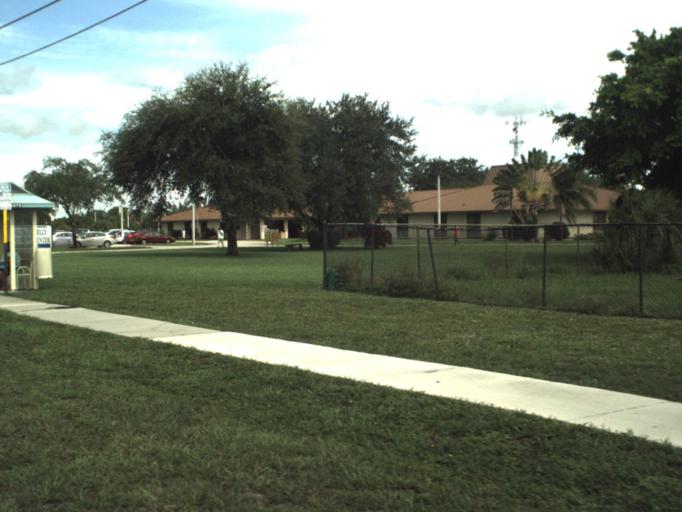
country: US
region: Florida
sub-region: Palm Beach County
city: Mangonia Park
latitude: 26.7533
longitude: -80.0663
